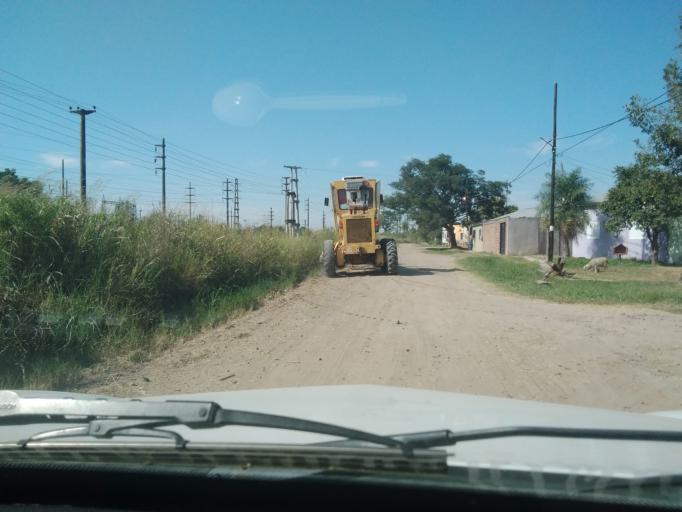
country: AR
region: Corrientes
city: Corrientes
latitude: -27.5117
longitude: -58.7991
